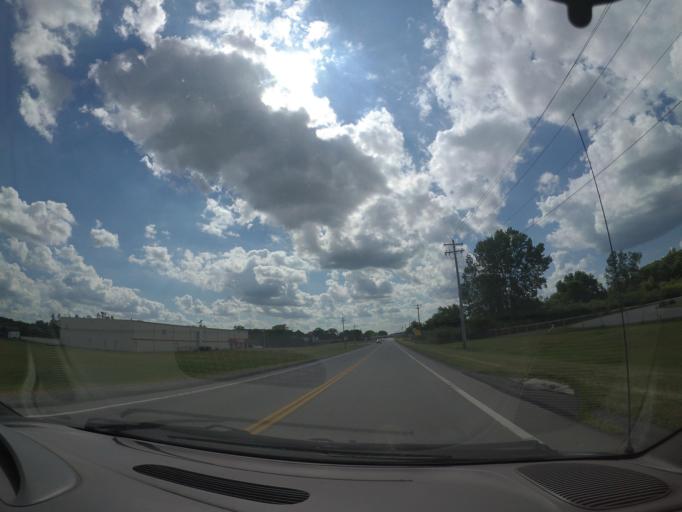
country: US
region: Ohio
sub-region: Huron County
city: Norwalk
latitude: 41.2496
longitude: -82.5674
